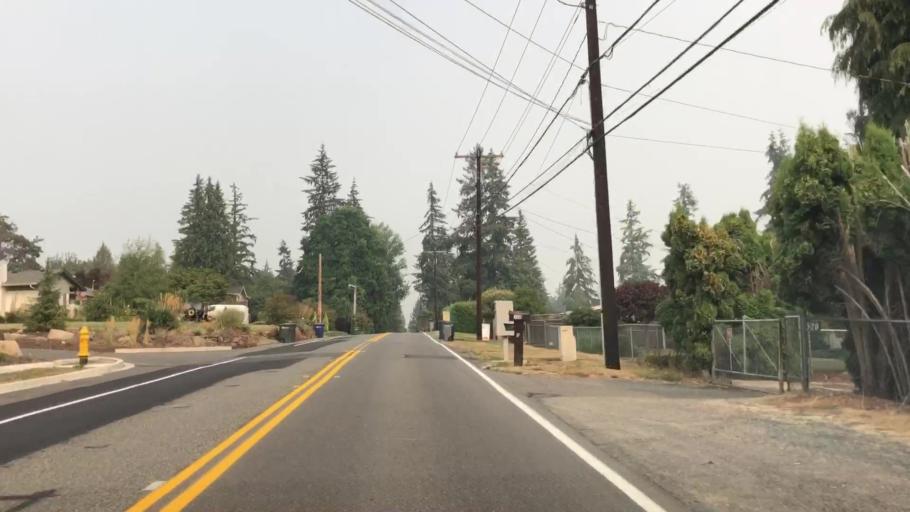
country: US
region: Washington
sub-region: King County
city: Kenmore
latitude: 47.7805
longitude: -122.2375
